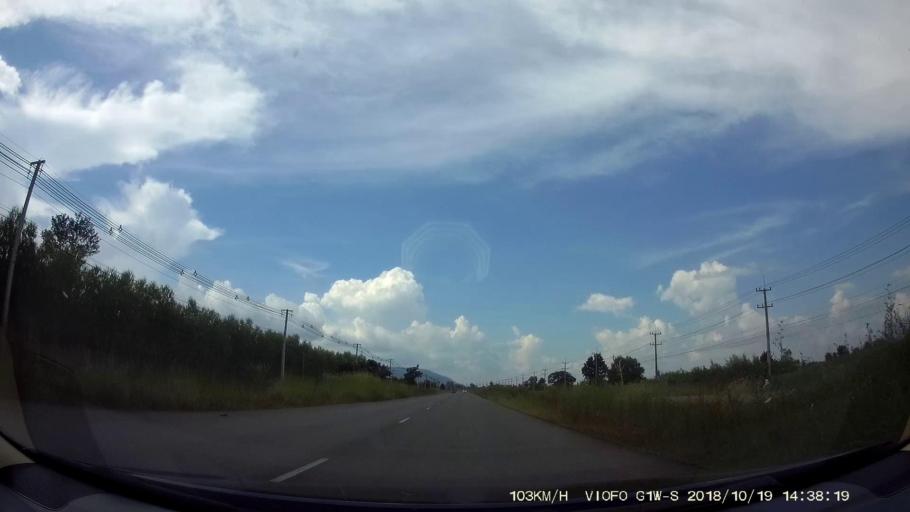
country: TH
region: Chaiyaphum
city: Kaeng Khro
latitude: 16.2113
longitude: 102.2025
